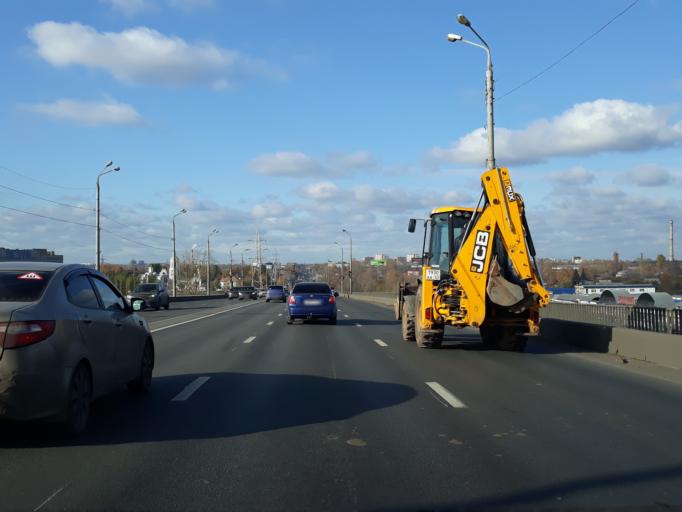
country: RU
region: Nizjnij Novgorod
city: Nizhniy Novgorod
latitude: 56.2526
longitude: 43.9432
